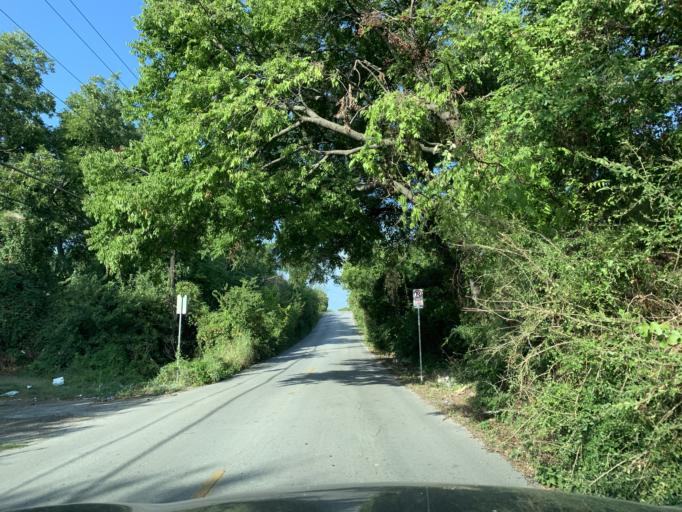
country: US
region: Texas
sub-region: Dallas County
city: Hutchins
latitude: 32.6775
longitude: -96.7675
